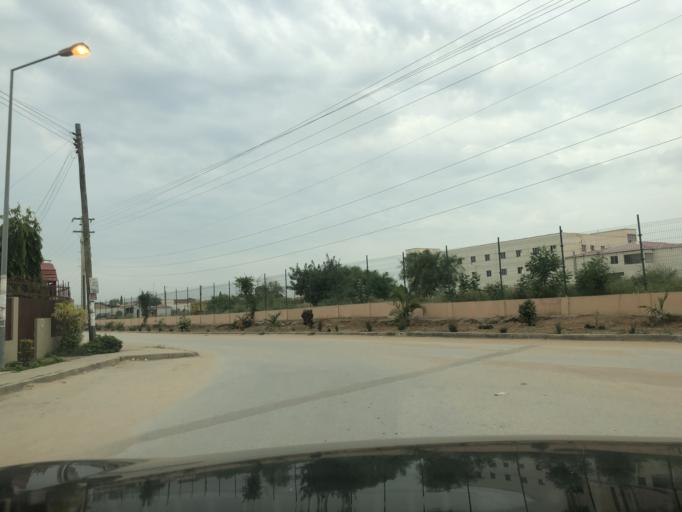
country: AO
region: Luanda
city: Luanda
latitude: -8.9408
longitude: 13.2504
